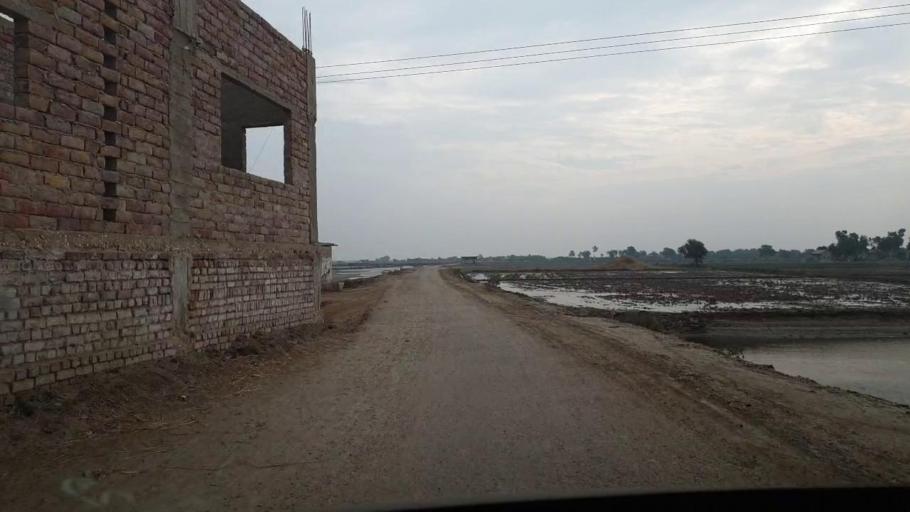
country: PK
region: Sindh
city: Chuhar Jamali
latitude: 24.4131
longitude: 67.9966
